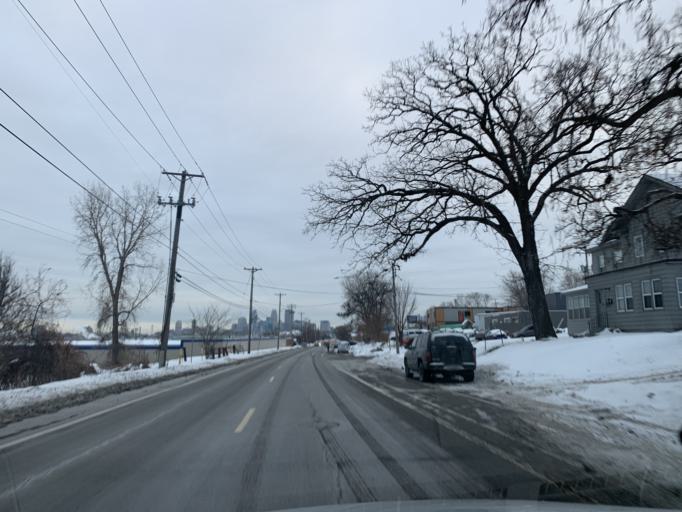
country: US
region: Minnesota
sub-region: Anoka County
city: Columbia Heights
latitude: 45.0172
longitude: -93.2812
